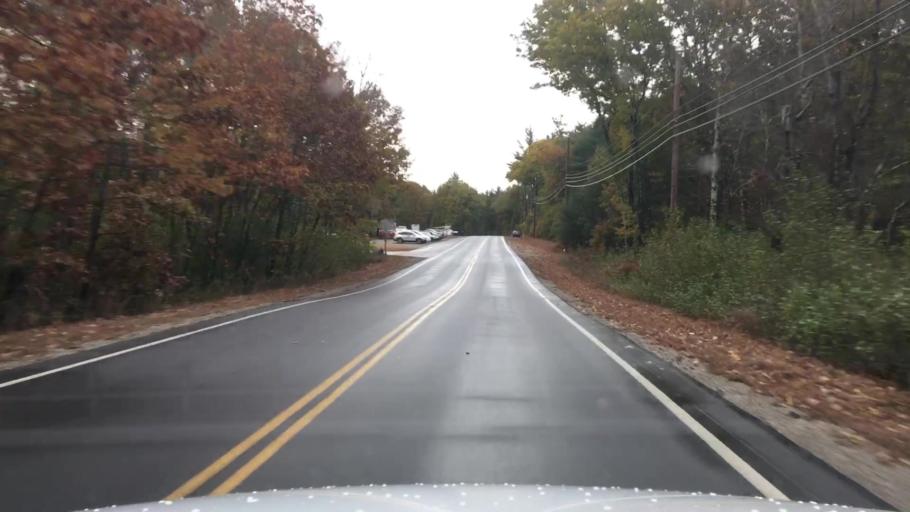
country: US
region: New Hampshire
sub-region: Strafford County
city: Lee
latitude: 43.1277
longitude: -71.0217
